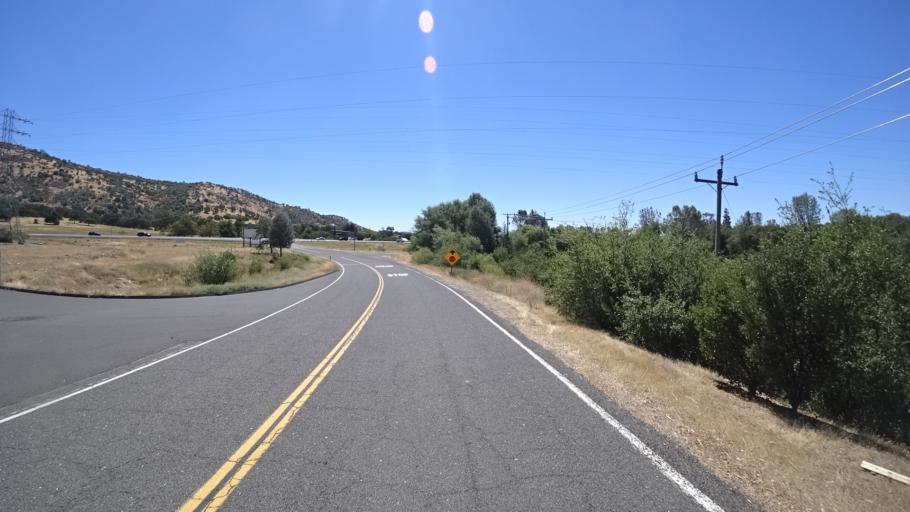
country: US
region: California
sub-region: Calaveras County
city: Copperopolis
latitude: 37.9836
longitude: -120.6474
